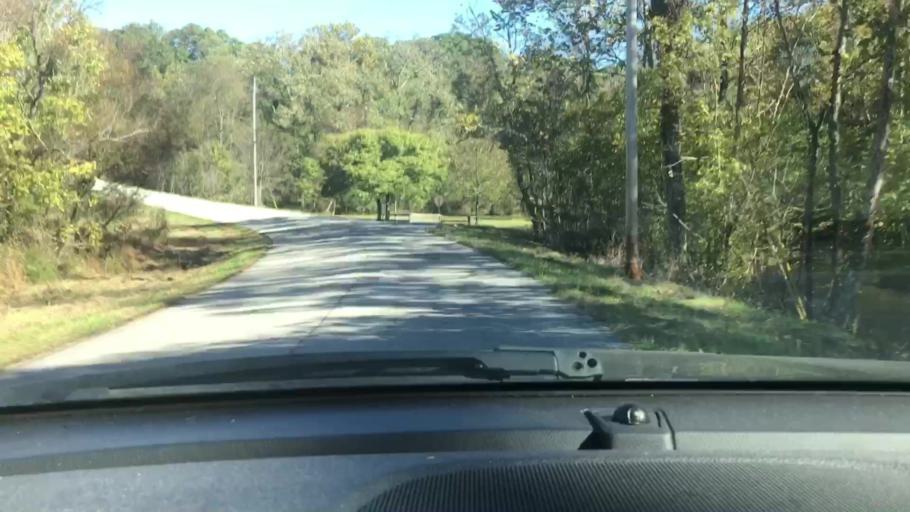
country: US
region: Tennessee
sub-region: Dickson County
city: Charlotte
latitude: 36.1796
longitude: -87.3057
